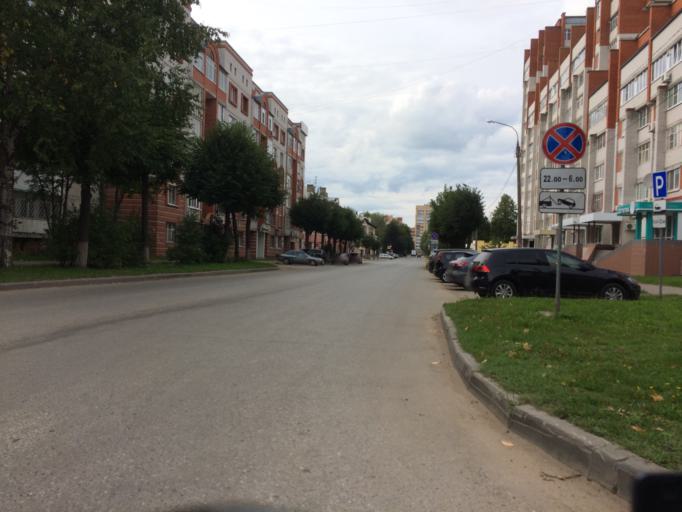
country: RU
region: Mariy-El
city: Yoshkar-Ola
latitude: 56.6368
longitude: 47.8692
